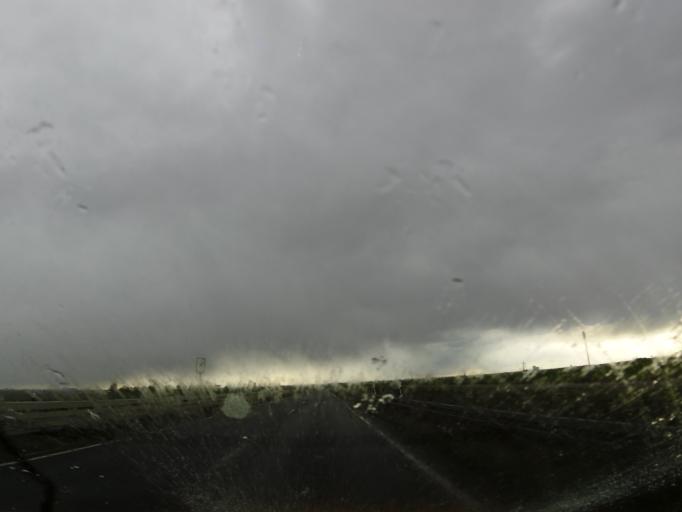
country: DE
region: Saxony-Anhalt
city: Wolmirsleben
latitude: 51.9812
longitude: 11.4779
